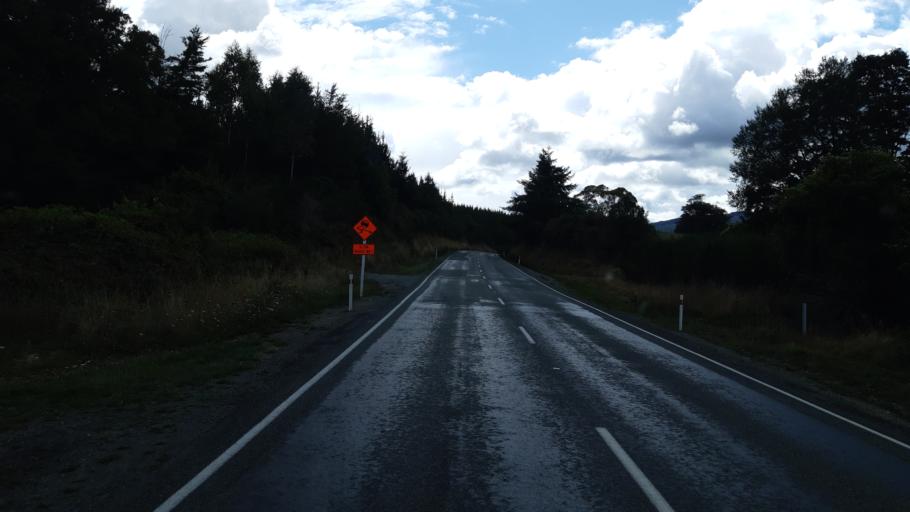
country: NZ
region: Tasman
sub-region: Tasman District
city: Wakefield
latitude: -41.5531
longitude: 172.7896
